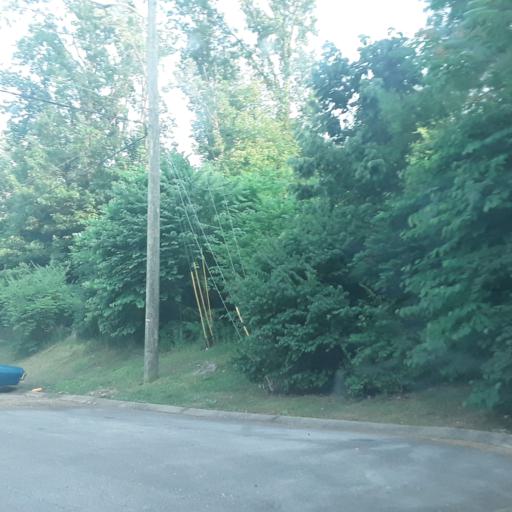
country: US
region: Tennessee
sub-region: Williamson County
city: Brentwood Estates
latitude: 36.0395
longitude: -86.7192
